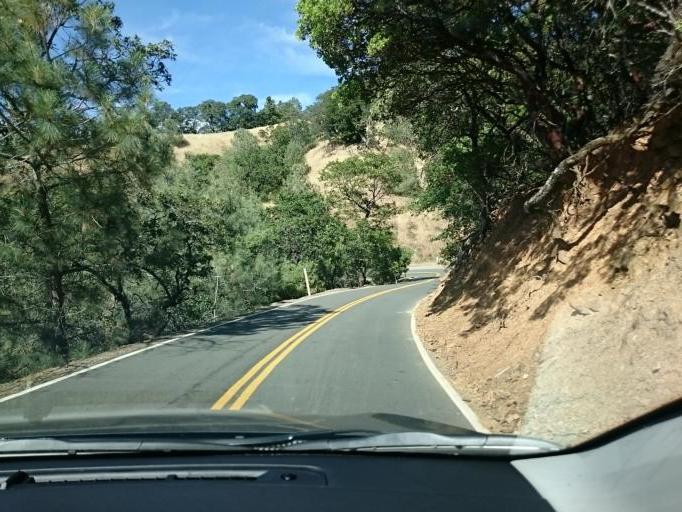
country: US
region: California
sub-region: Santa Clara County
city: East Foothills
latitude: 37.3410
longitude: -121.6632
